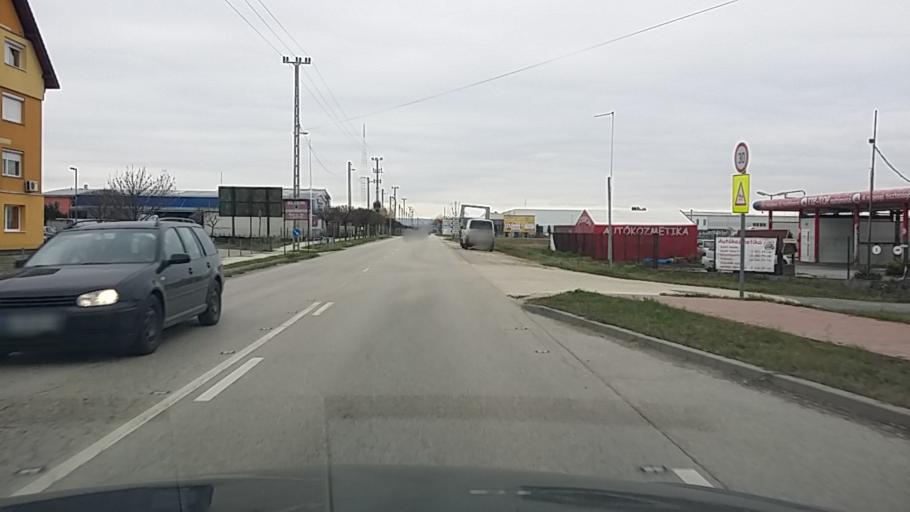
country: HU
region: Pest
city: Szigetszentmiklos
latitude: 47.3608
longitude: 19.0276
